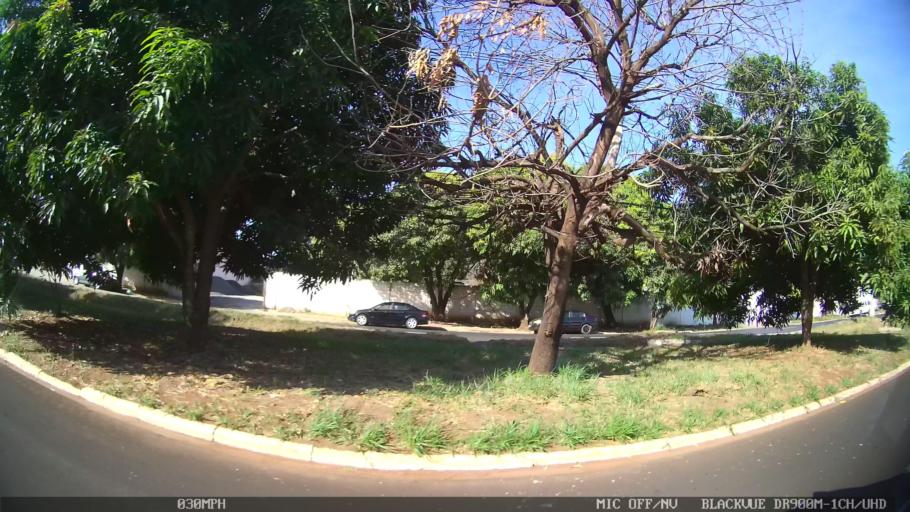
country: BR
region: Sao Paulo
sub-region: Ribeirao Preto
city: Ribeirao Preto
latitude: -21.1857
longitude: -47.7611
